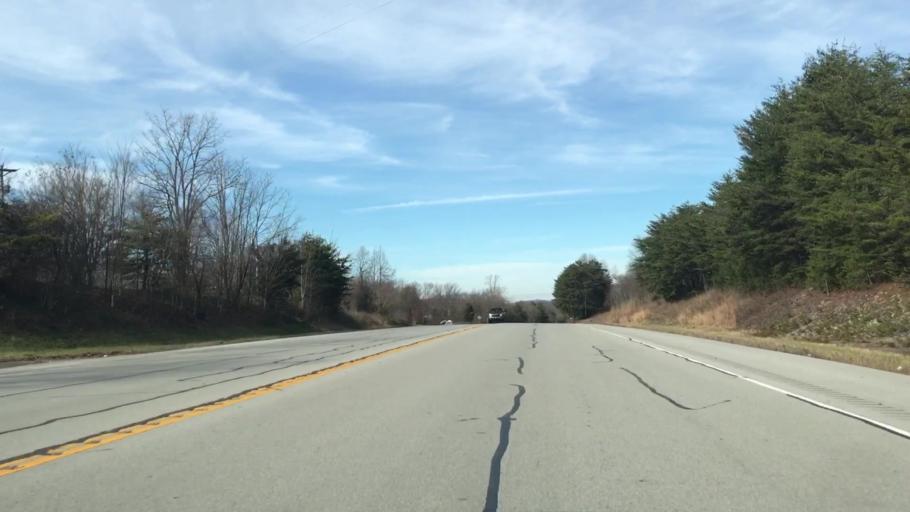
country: US
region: Kentucky
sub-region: McCreary County
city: Whitley City
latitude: 36.8686
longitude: -84.4898
